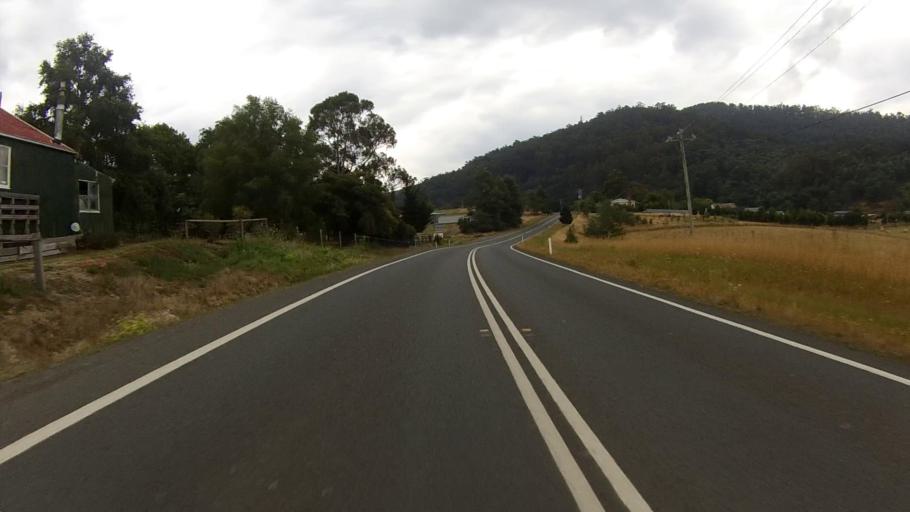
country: AU
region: Tasmania
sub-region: Huon Valley
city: Cygnet
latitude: -43.1442
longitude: 147.0644
